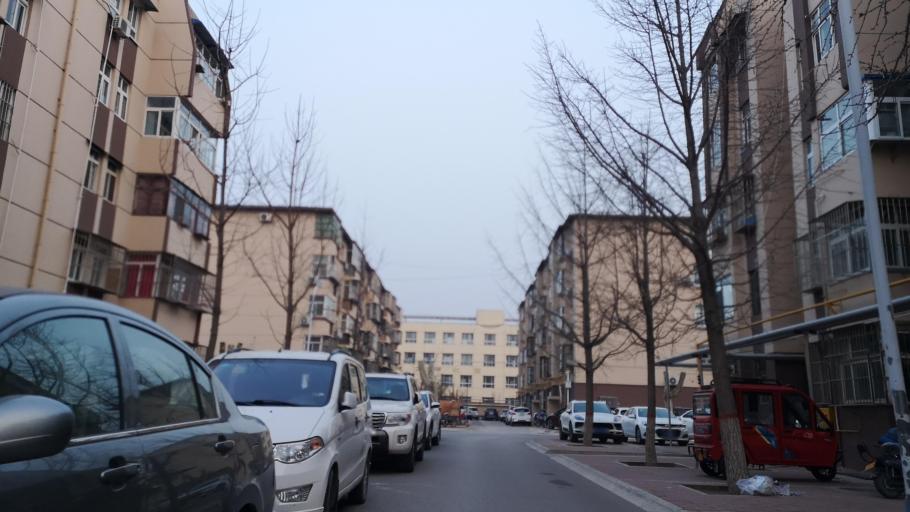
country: CN
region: Henan Sheng
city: Zhongyuanlu
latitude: 35.7831
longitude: 115.0739
